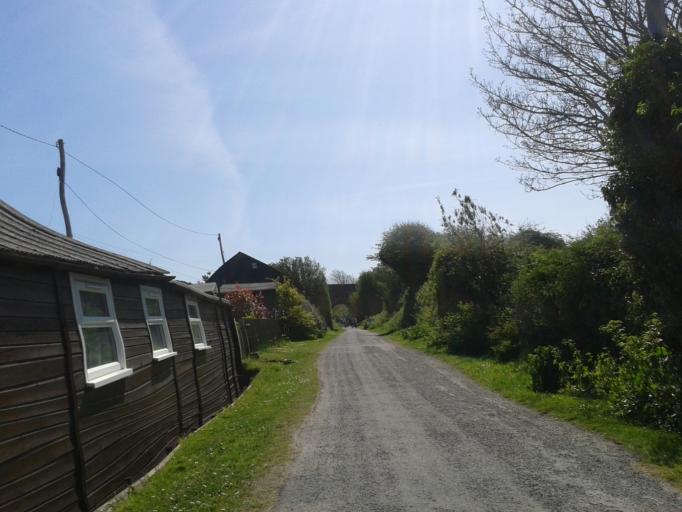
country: GB
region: England
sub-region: Devon
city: Appledore
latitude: 51.0585
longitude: -4.1776
